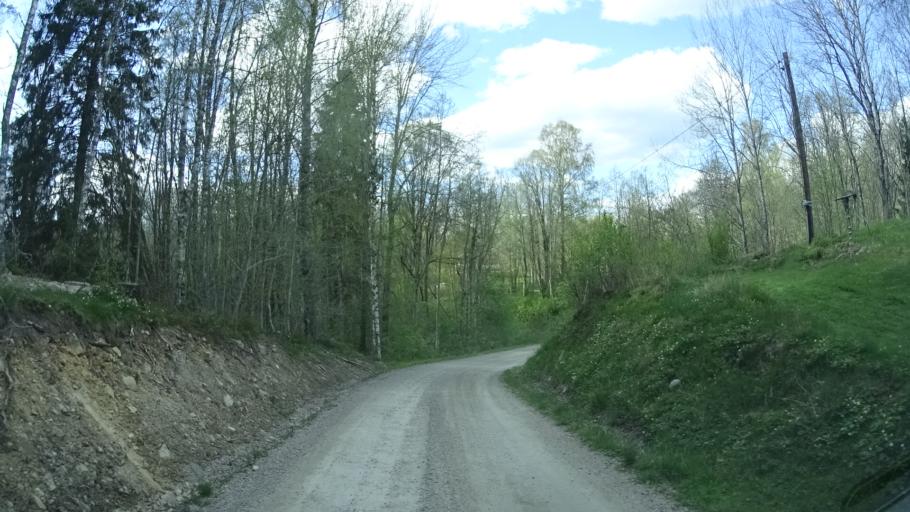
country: SE
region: OErebro
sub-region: Orebro Kommun
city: Garphyttan
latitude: 59.4280
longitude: 14.8613
